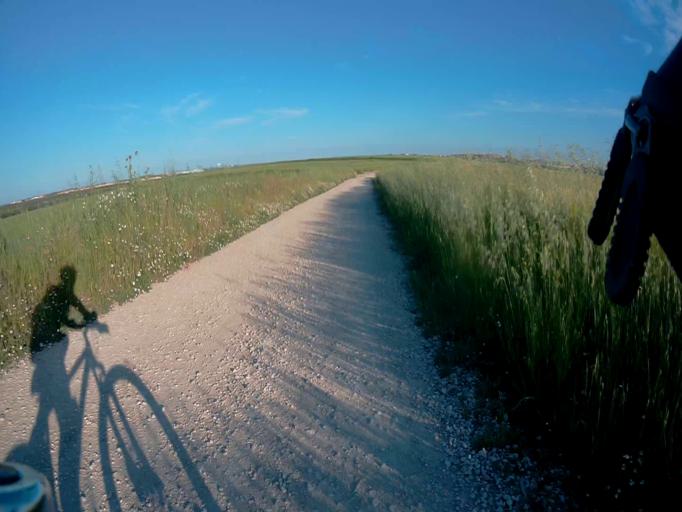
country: ES
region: Madrid
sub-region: Provincia de Madrid
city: Alcorcon
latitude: 40.3228
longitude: -3.8135
